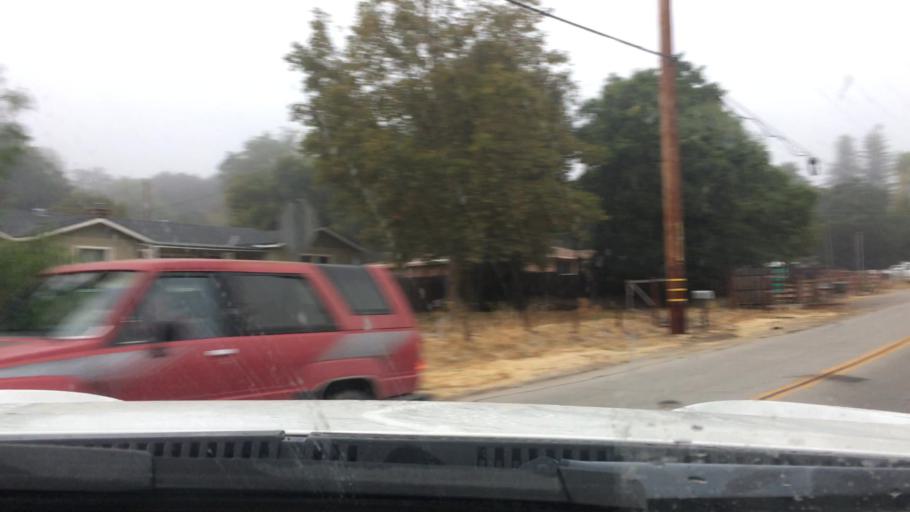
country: US
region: California
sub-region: San Luis Obispo County
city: Atascadero
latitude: 35.4831
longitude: -120.6837
